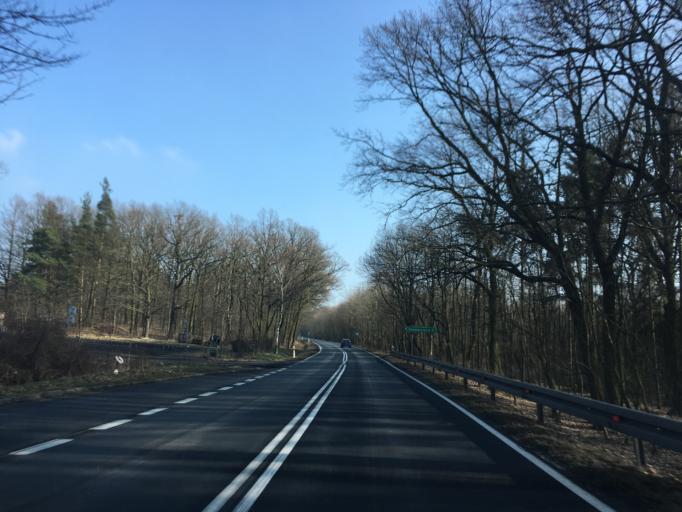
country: PL
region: Lower Silesian Voivodeship
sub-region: Powiat legnicki
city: Chojnow
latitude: 51.2751
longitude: 15.8744
